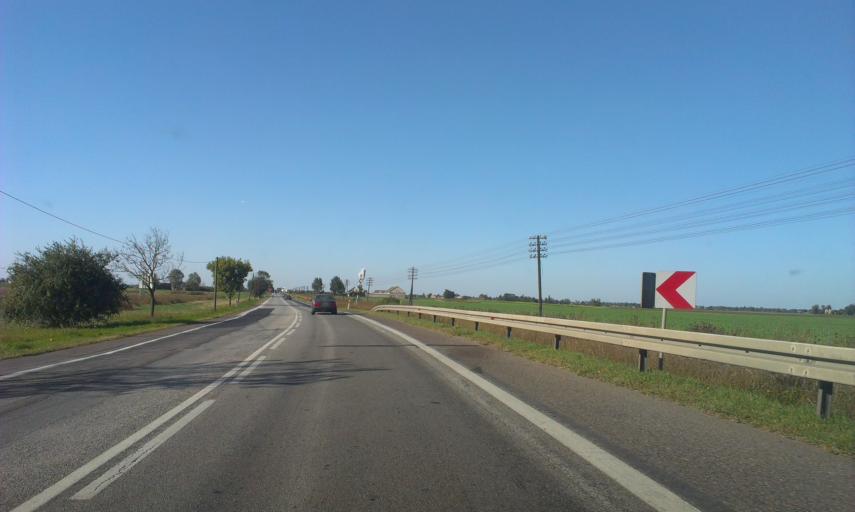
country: PL
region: Kujawsko-Pomorskie
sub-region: Powiat torunski
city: Lysomice
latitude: 53.1248
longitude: 18.6272
